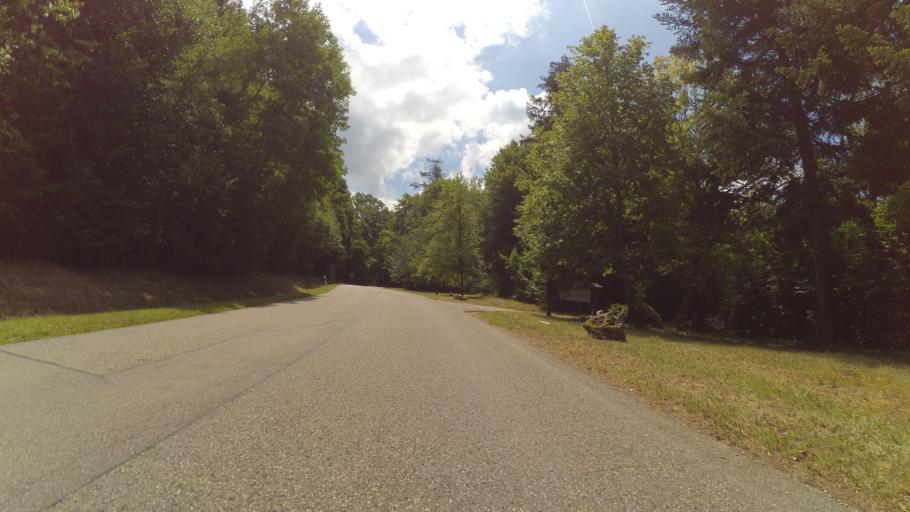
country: DE
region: Baden-Wuerttemberg
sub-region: Freiburg Region
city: Badenweiler
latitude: 47.7944
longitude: 7.6679
